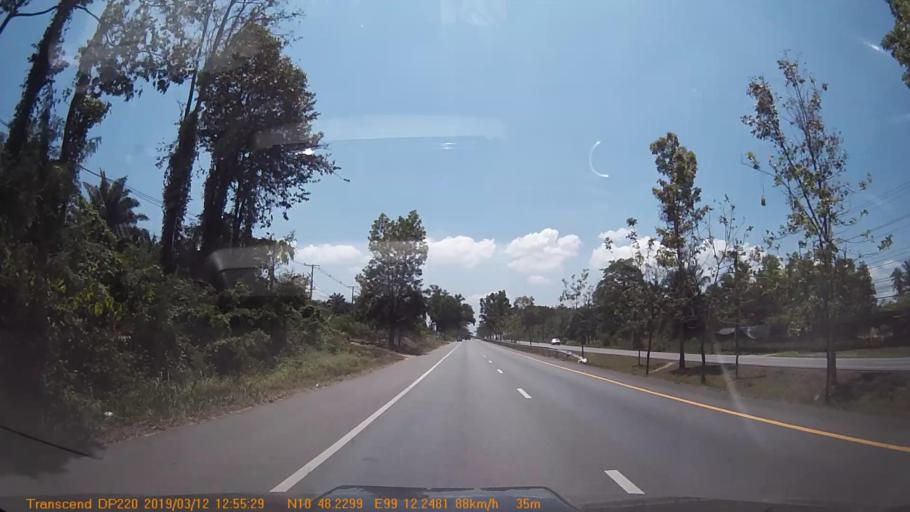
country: TH
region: Chumphon
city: Tha Sae
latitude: 10.8036
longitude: 99.2040
